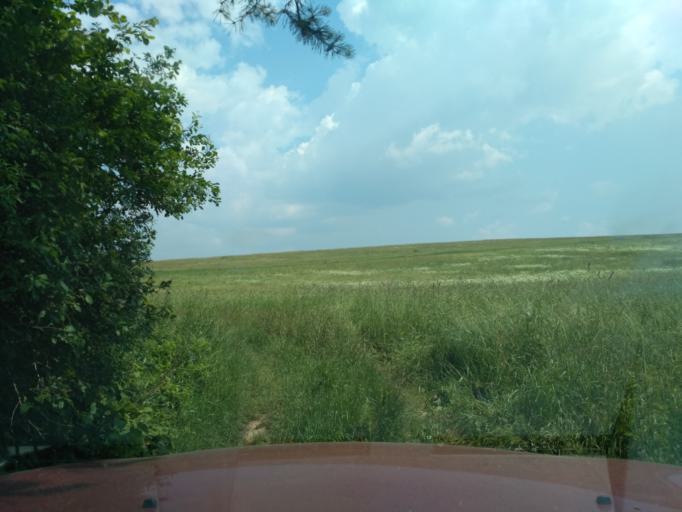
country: SK
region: Kosicky
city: Moldava nad Bodvou
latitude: 48.6221
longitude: 21.0470
